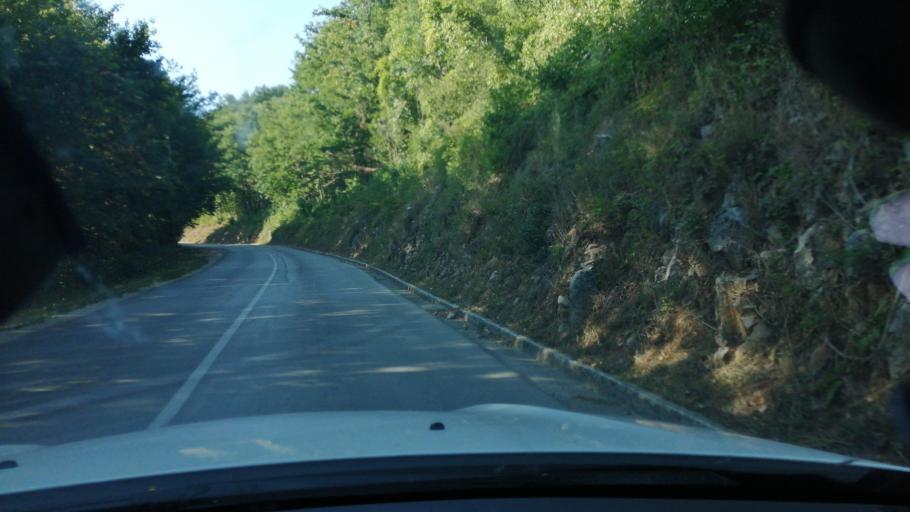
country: RS
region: Central Serbia
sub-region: Moravicki Okrug
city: Ivanjica
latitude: 43.6386
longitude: 20.2407
